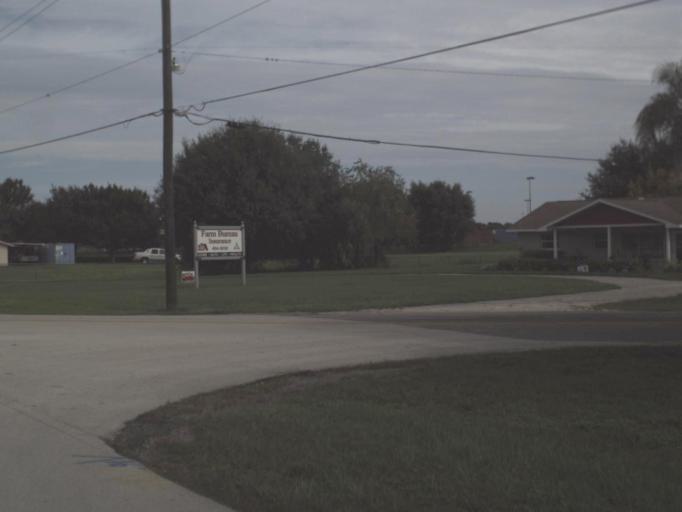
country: US
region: Florida
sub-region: DeSoto County
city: Southeast Arcadia
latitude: 27.2048
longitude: -81.8311
